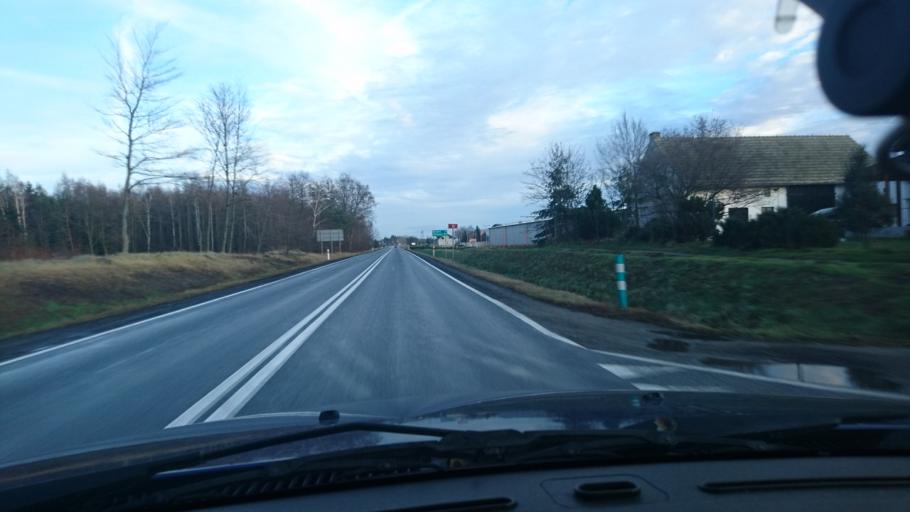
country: PL
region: Greater Poland Voivodeship
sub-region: Powiat kepinski
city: Leka Opatowska
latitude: 51.2248
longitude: 18.0956
